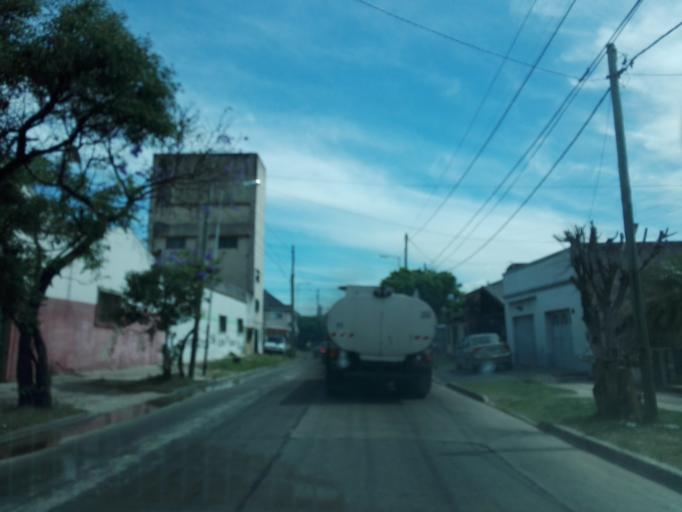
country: AR
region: Buenos Aires
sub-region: Partido de Avellaneda
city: Avellaneda
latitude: -34.6884
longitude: -58.3512
